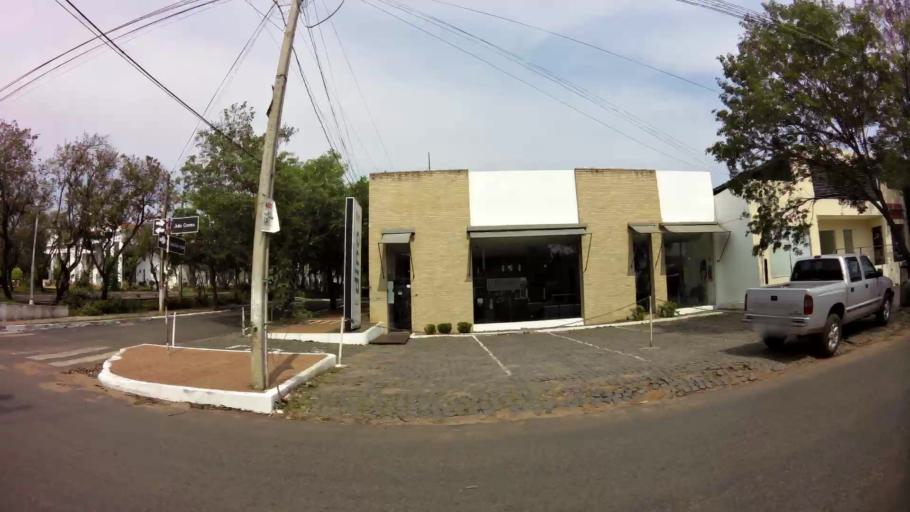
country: PY
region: Asuncion
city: Asuncion
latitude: -25.2729
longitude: -57.5657
